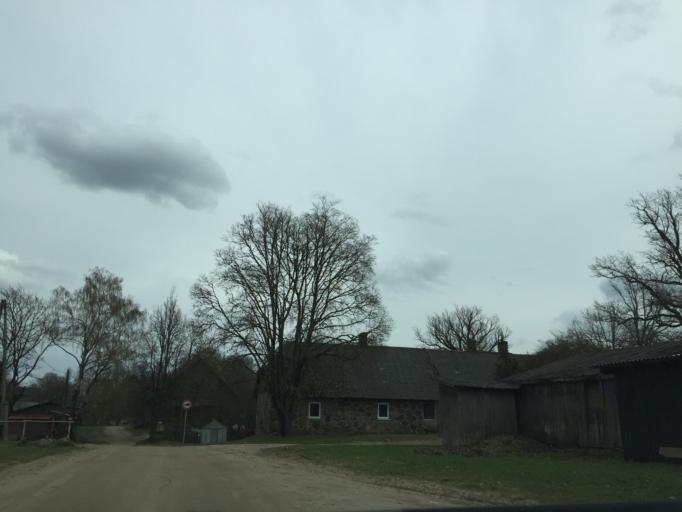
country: LV
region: Priekuli
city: Priekuli
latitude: 57.3151
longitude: 25.3617
